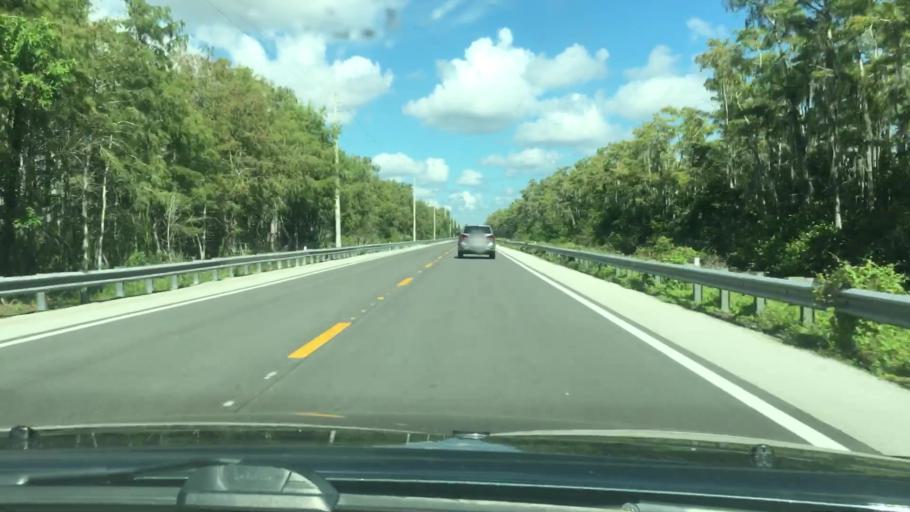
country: US
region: Florida
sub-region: Miami-Dade County
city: Kendall West
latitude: 25.7976
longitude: -80.8650
